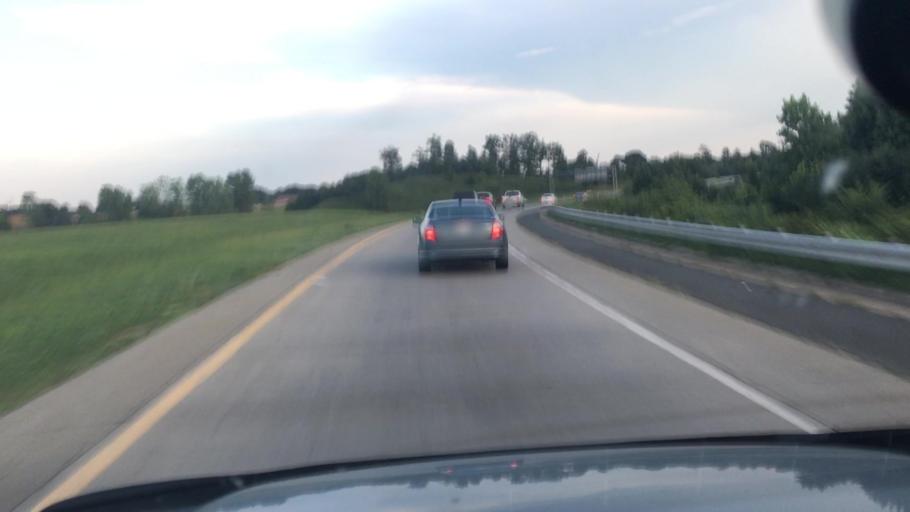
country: US
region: North Carolina
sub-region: Gaston County
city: Belmont
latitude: 35.2474
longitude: -80.9708
